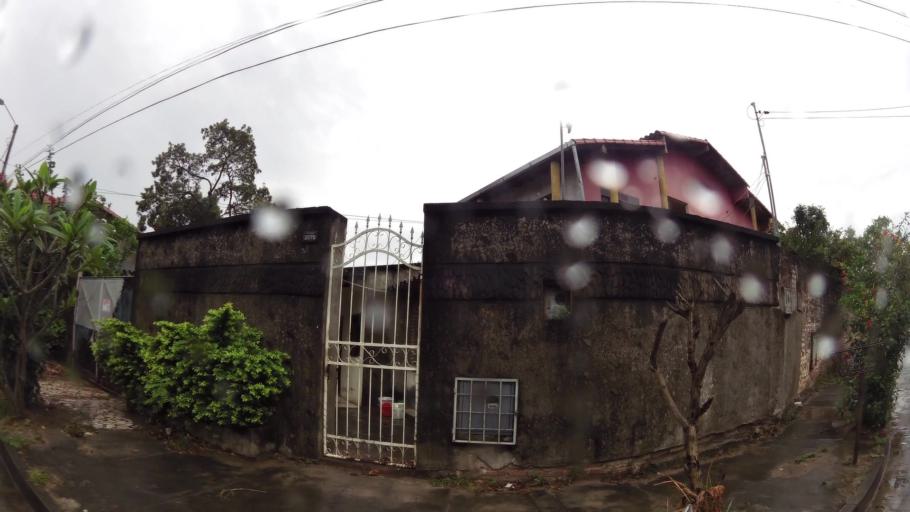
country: BO
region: Santa Cruz
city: Santa Cruz de la Sierra
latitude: -17.7981
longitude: -63.1577
